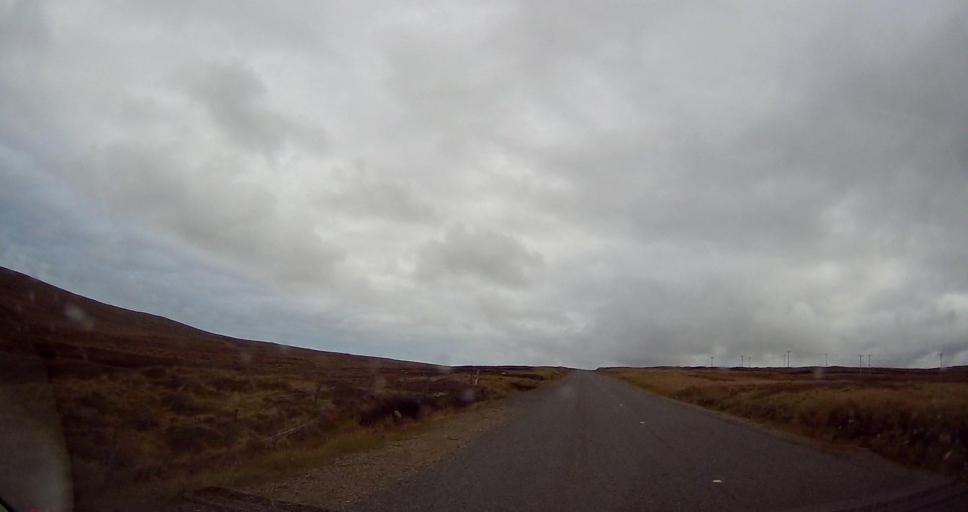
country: GB
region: Scotland
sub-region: Shetland Islands
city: Shetland
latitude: 60.6204
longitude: -1.0750
